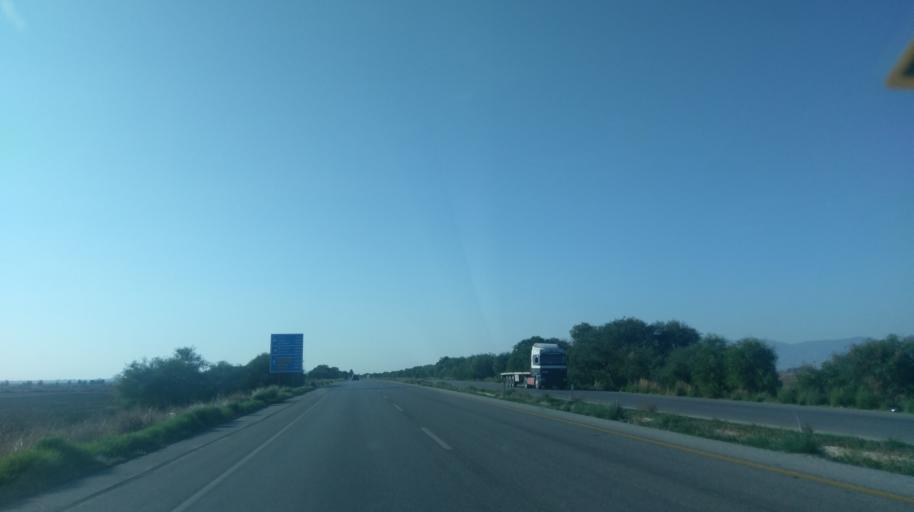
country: CY
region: Ammochostos
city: Lefkonoiko
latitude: 35.1815
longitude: 33.7130
